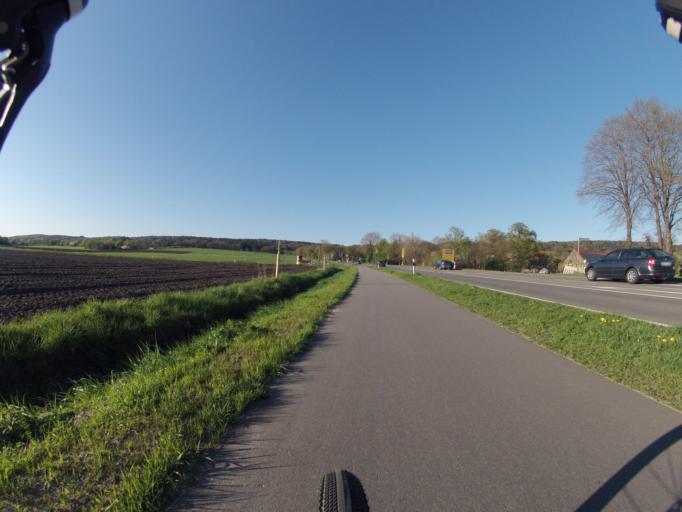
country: DE
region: North Rhine-Westphalia
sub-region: Regierungsbezirk Munster
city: Birgte
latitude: 52.2378
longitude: 7.6933
